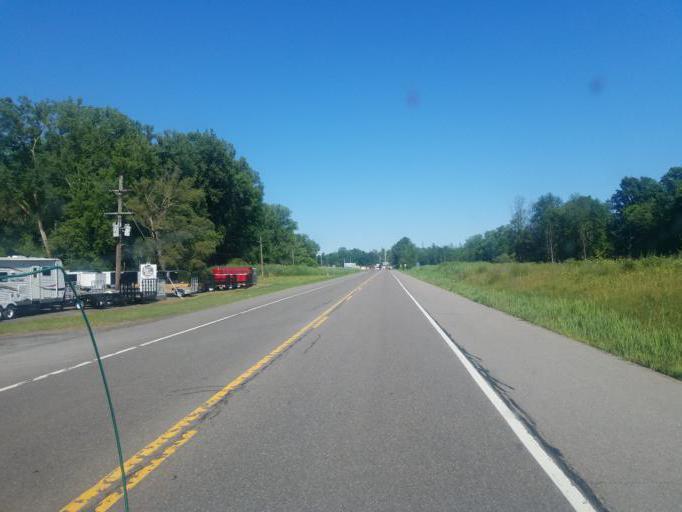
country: US
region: New York
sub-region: Wayne County
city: Lyons
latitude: 43.0592
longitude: -77.0122
